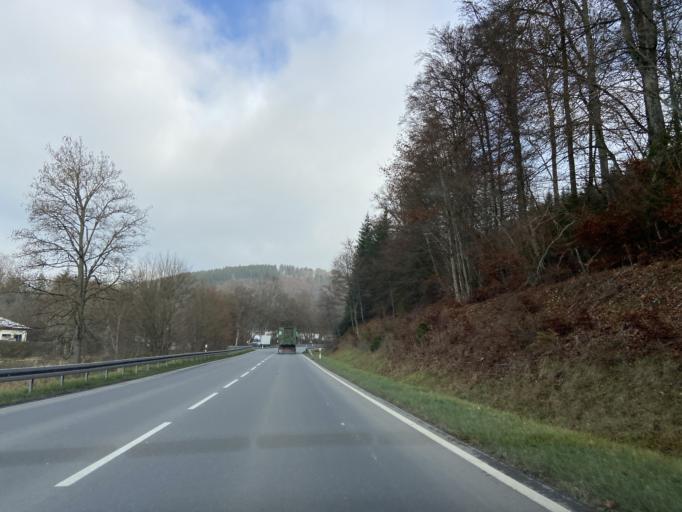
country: DE
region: Baden-Wuerttemberg
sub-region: Tuebingen Region
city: Veringenstadt
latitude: 48.1838
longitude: 9.2170
